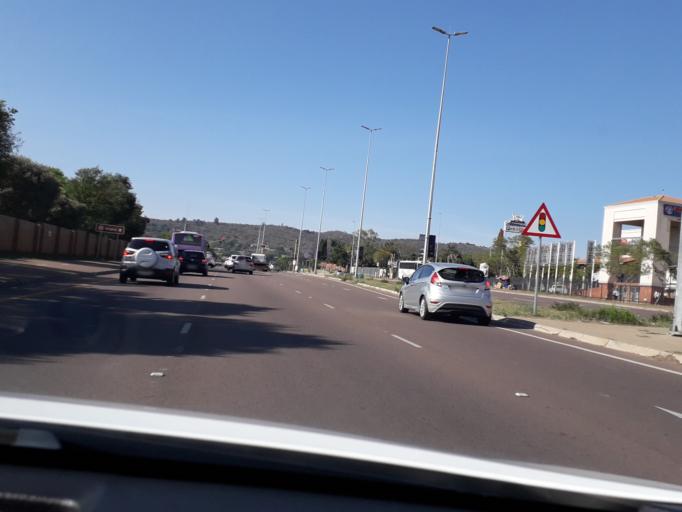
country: ZA
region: Gauteng
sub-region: City of Tshwane Metropolitan Municipality
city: Pretoria
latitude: -25.7572
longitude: 28.3237
